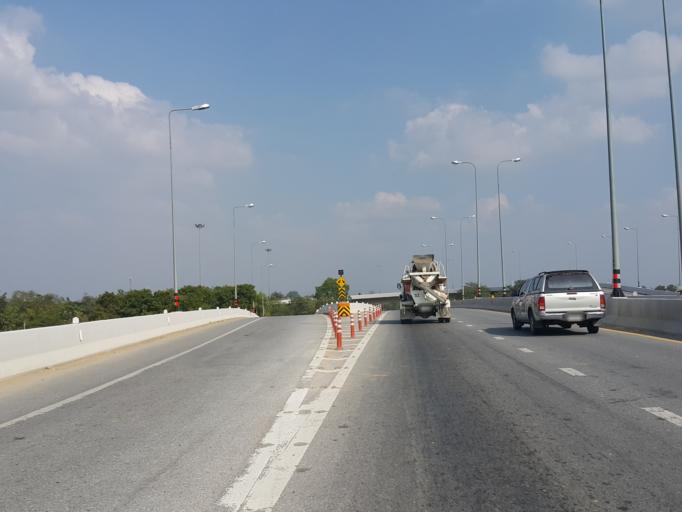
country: TH
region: Chiang Mai
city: Saraphi
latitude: 18.7526
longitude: 99.0317
